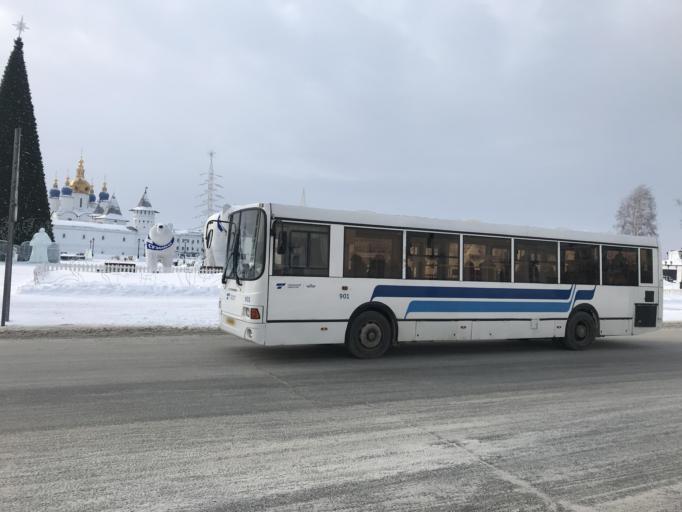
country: RU
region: Tjumen
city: Tobol'sk
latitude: 58.2012
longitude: 68.2543
